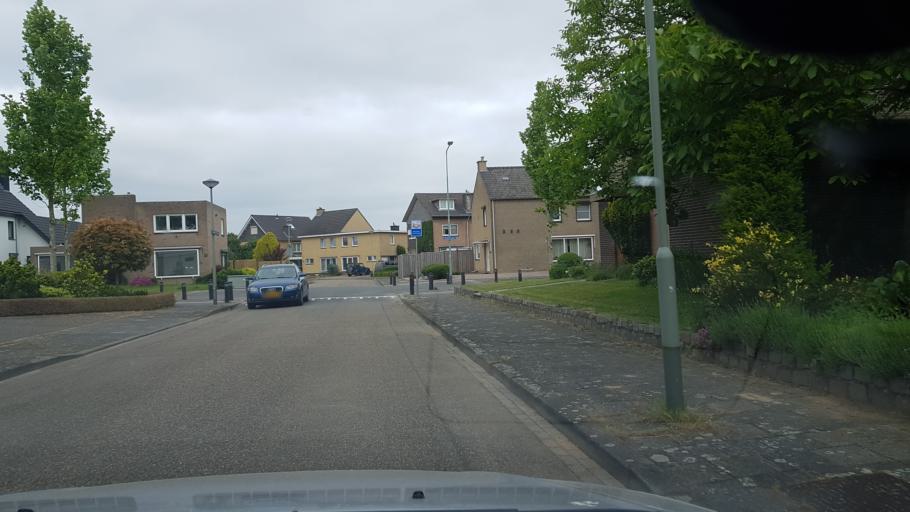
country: NL
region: Limburg
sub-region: Gemeente Stein
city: Stein
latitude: 50.9721
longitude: 5.7694
